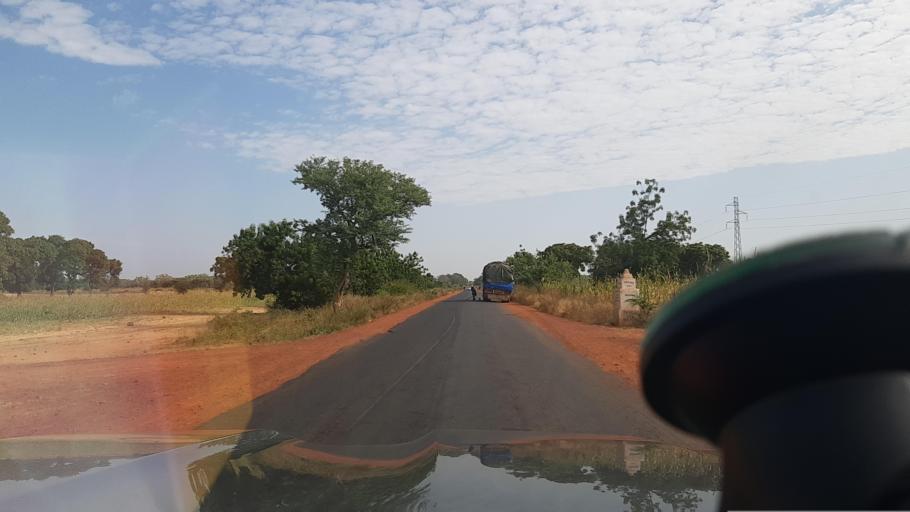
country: ML
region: Segou
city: Segou
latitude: 13.5213
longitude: -6.1344
